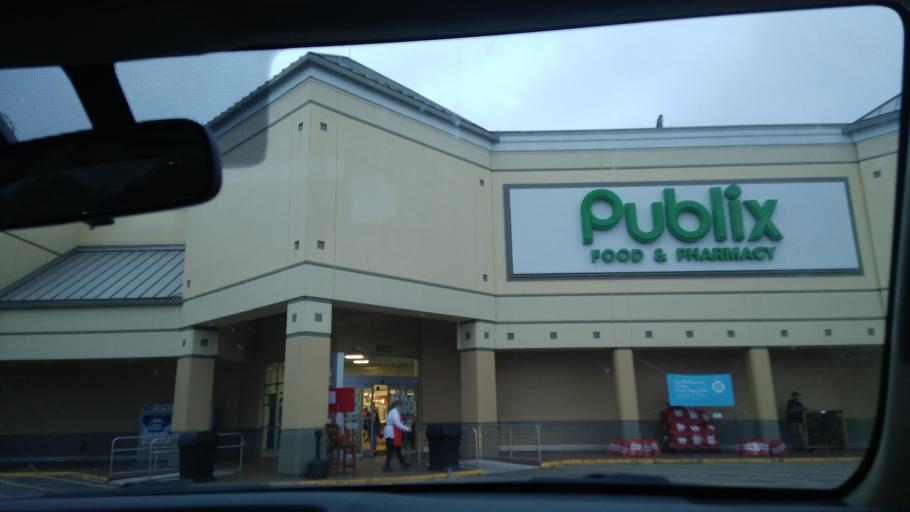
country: US
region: Florida
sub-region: Polk County
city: Lake Wales
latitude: 27.8931
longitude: -81.5889
